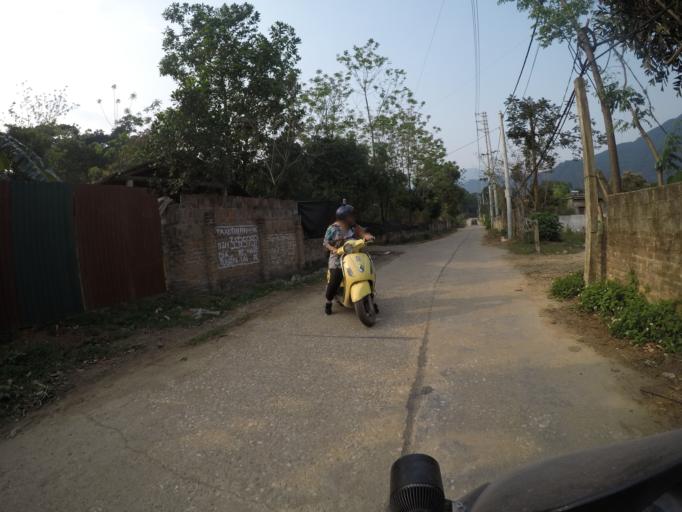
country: VN
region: Vinh Phuc
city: Trai Ngau
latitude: 21.4674
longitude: 105.5708
